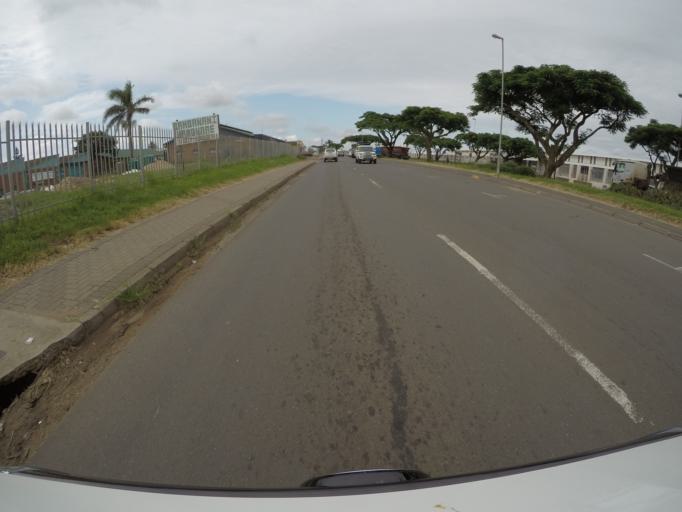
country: ZA
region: KwaZulu-Natal
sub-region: uThungulu District Municipality
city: Empangeni
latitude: -28.7765
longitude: 31.9005
